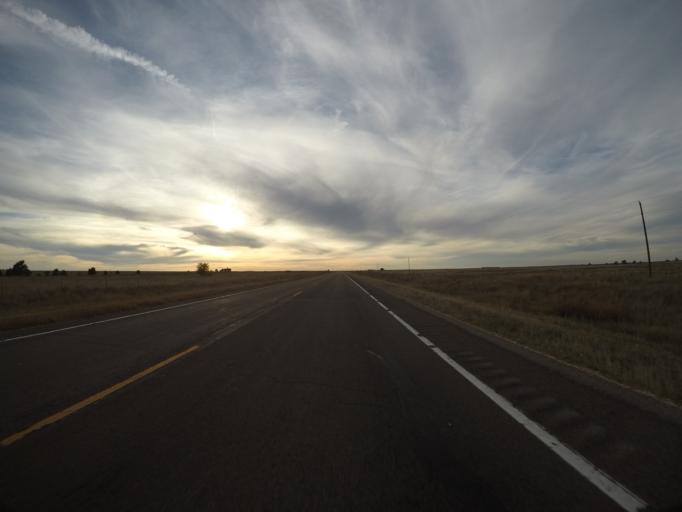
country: US
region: Colorado
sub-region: Yuma County
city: Yuma
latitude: 39.6702
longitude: -102.8877
